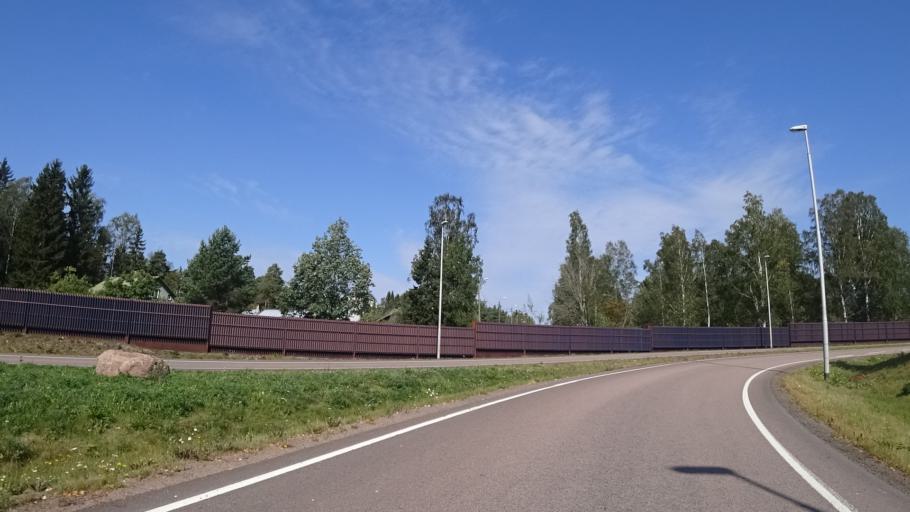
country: FI
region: Kymenlaakso
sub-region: Kotka-Hamina
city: Hamina
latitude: 60.5661
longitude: 27.1581
